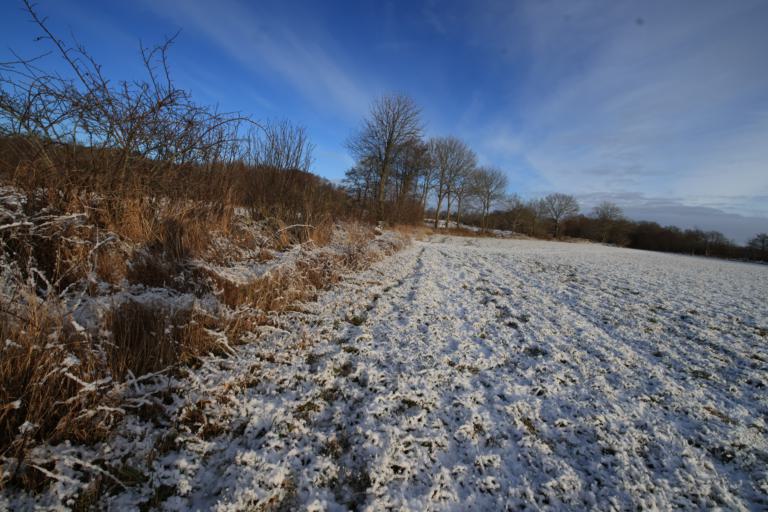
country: SE
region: Halland
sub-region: Varbergs Kommun
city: Varberg
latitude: 57.1336
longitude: 12.2872
